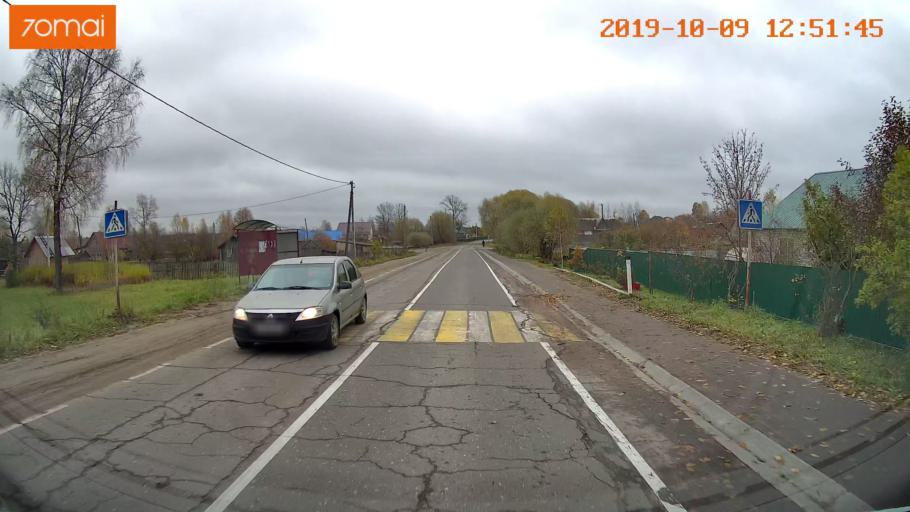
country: RU
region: Jaroslavl
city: Prechistoye
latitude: 58.4178
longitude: 40.3461
